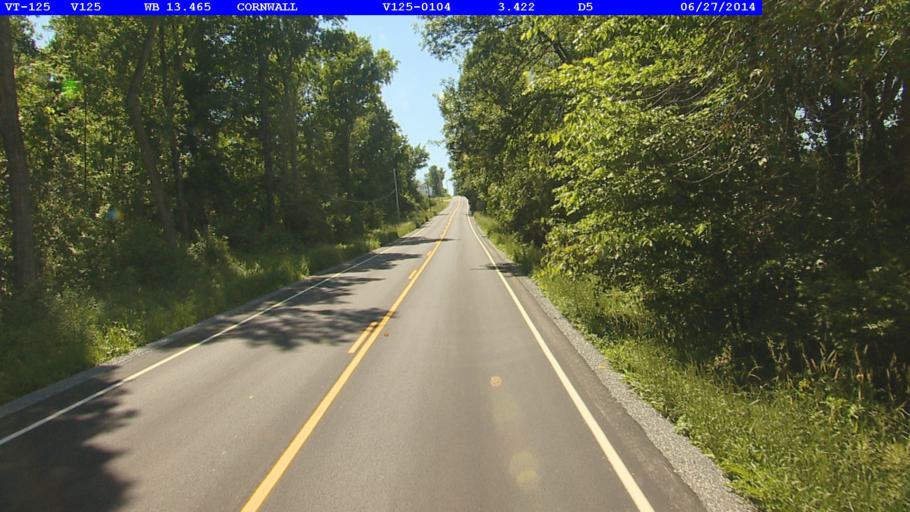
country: US
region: Vermont
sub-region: Addison County
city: Middlebury (village)
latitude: 44.0077
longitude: -73.2055
